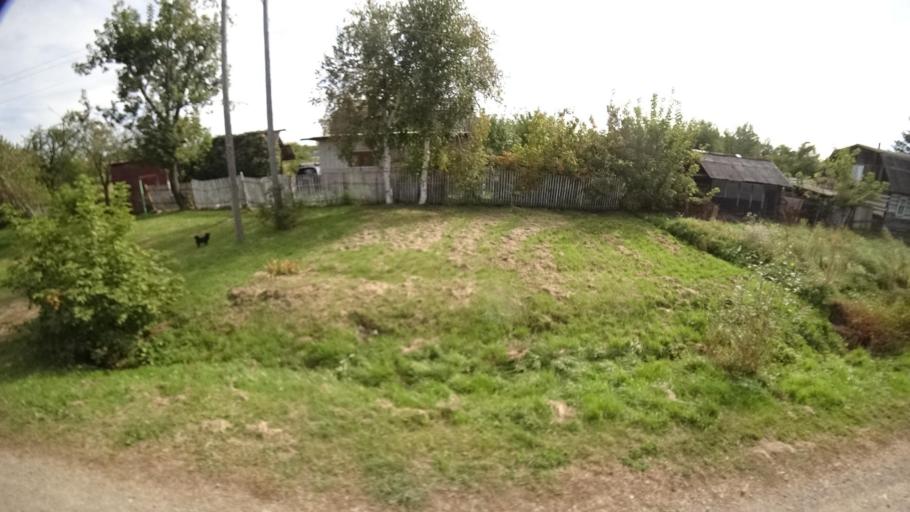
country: RU
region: Primorskiy
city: Dostoyevka
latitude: 44.3285
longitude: 133.4831
